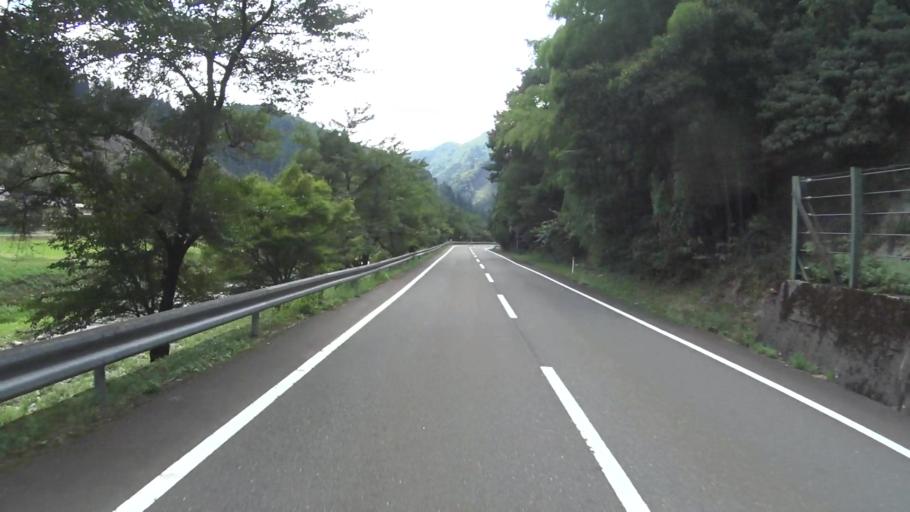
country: JP
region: Fukui
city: Obama
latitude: 35.3351
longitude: 135.5747
